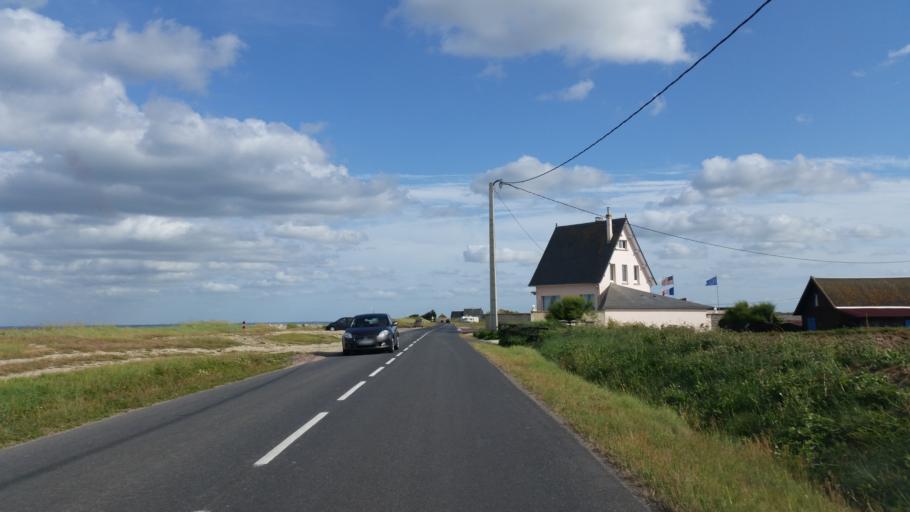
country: FR
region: Lower Normandy
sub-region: Departement de la Manche
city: Sainte-Mere-Eglise
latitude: 49.4540
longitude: -1.2209
